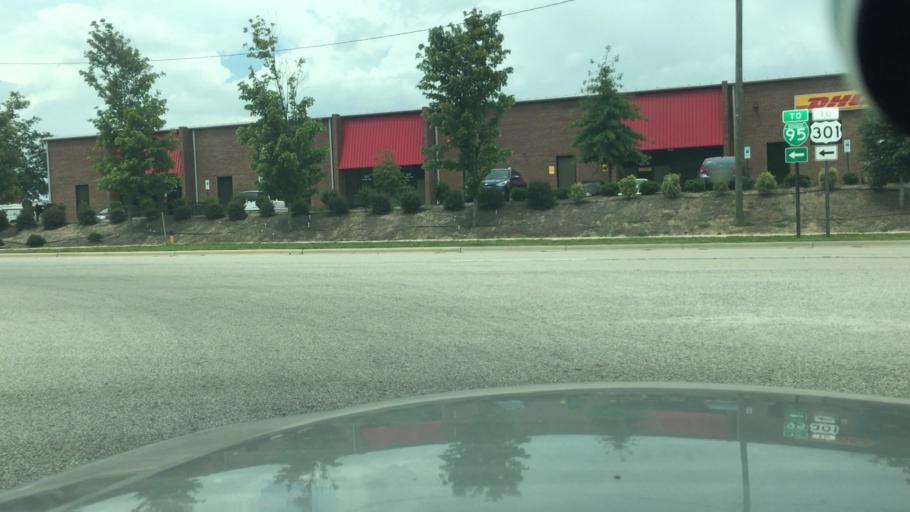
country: US
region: North Carolina
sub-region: Cumberland County
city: Fayetteville
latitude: 34.9964
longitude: -78.8915
